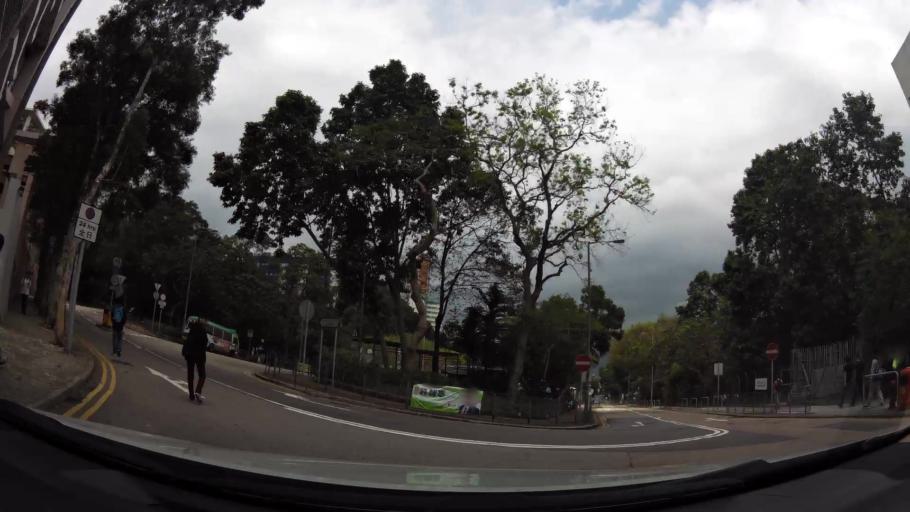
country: HK
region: Wanchai
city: Wan Chai
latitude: 22.2829
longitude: 114.1989
